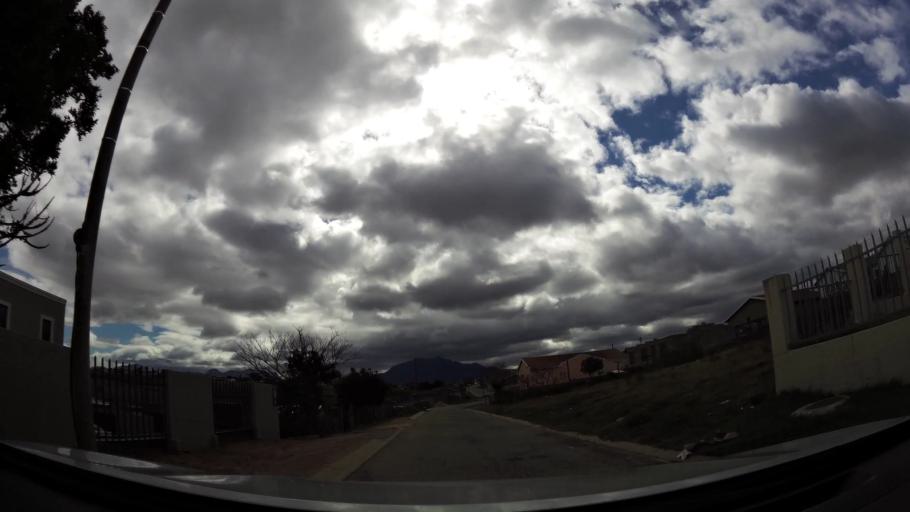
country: ZA
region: Western Cape
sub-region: Eden District Municipality
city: George
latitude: -34.0261
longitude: 22.4749
